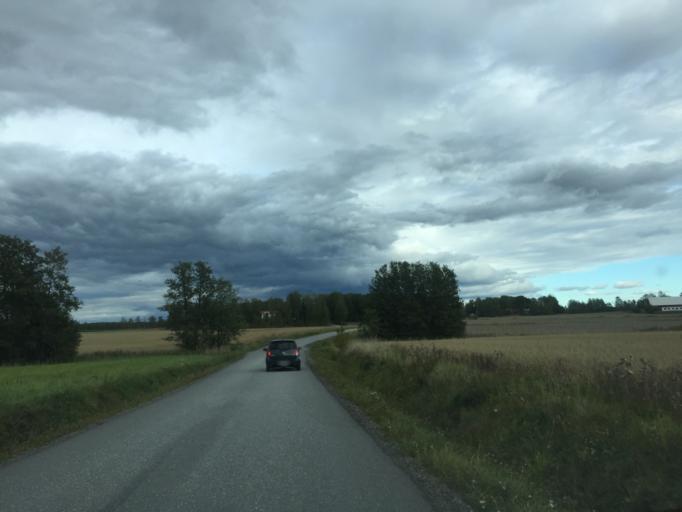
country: SE
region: OErebro
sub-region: Orebro Kommun
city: Hovsta
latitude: 59.3208
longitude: 15.1955
